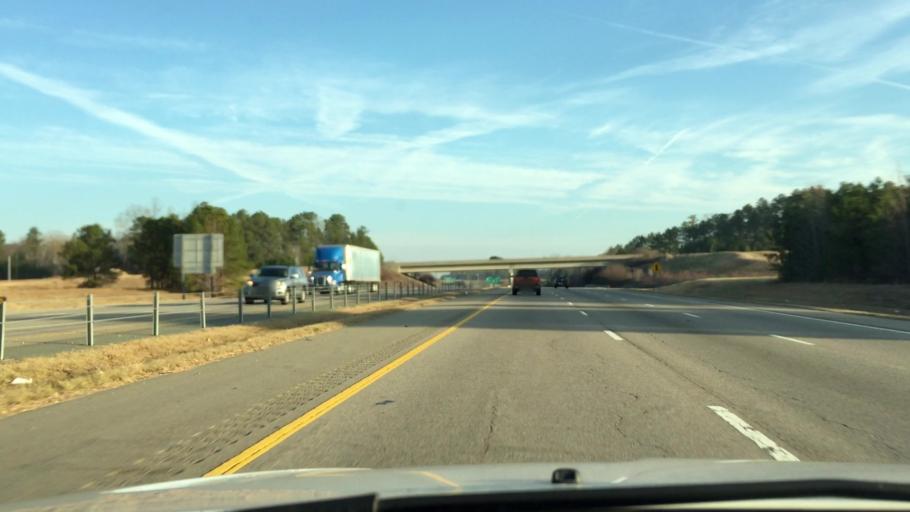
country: US
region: North Carolina
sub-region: Lee County
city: Sanford
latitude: 35.5007
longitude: -79.1922
